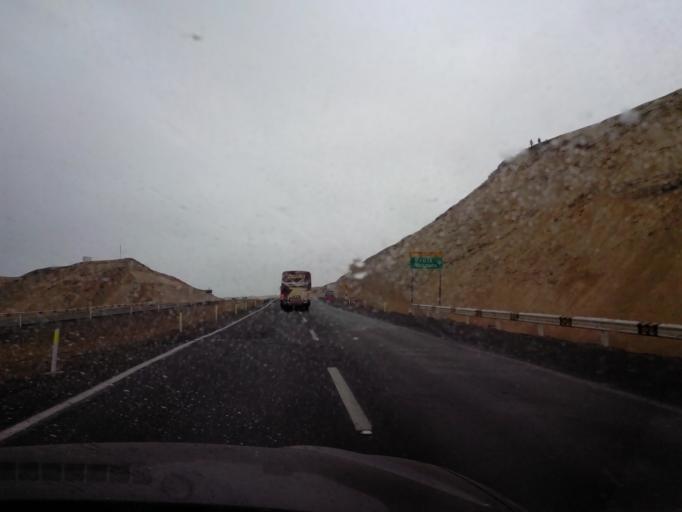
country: PE
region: Ica
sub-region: Provincia de Chincha
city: San Pedro
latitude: -13.2983
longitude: -76.2576
